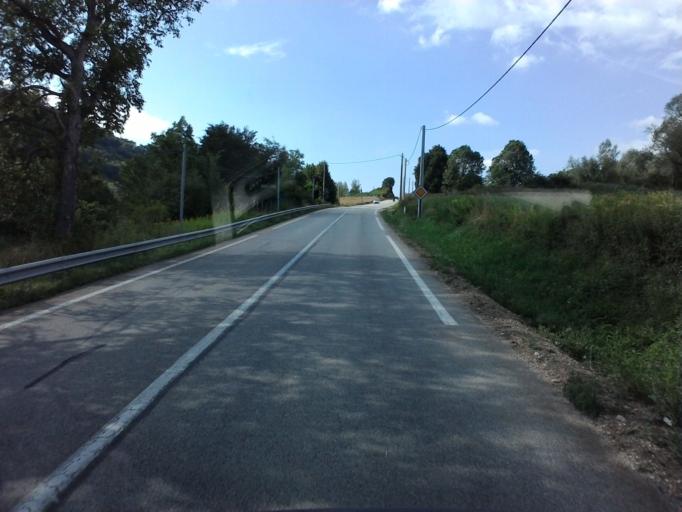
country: FR
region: Rhone-Alpes
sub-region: Departement de l'Isere
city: Chirens
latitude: 45.4331
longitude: 5.5660
